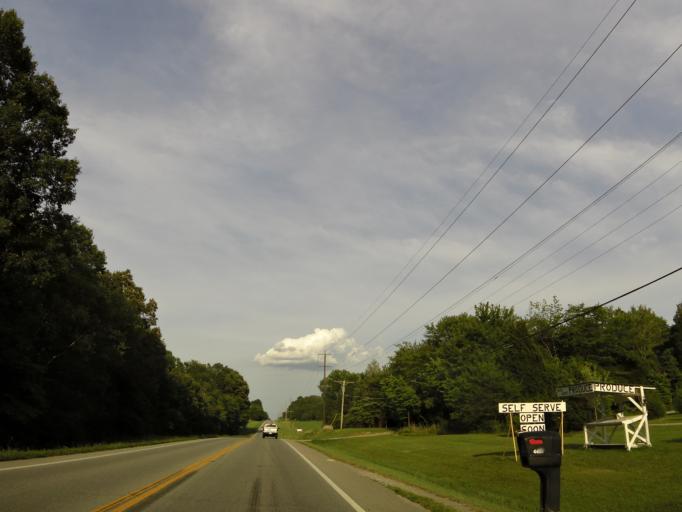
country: US
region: Tennessee
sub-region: Humphreys County
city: McEwen
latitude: 36.0910
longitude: -87.5121
